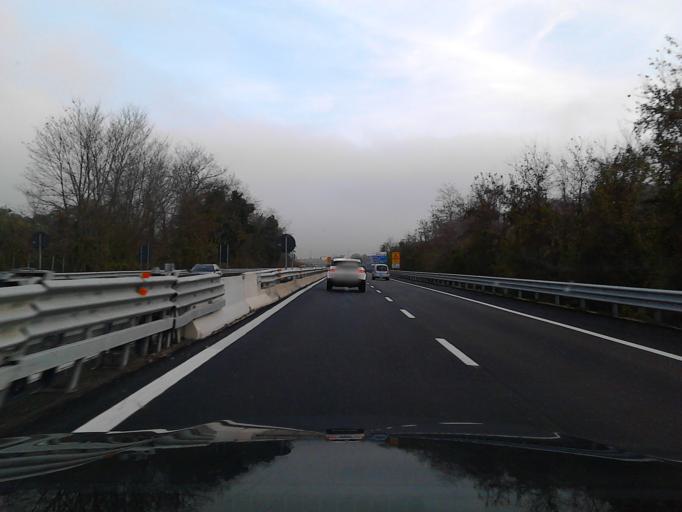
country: IT
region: Abruzzo
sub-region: Provincia di Chieti
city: Francavilla al Mare
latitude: 42.4031
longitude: 14.2760
